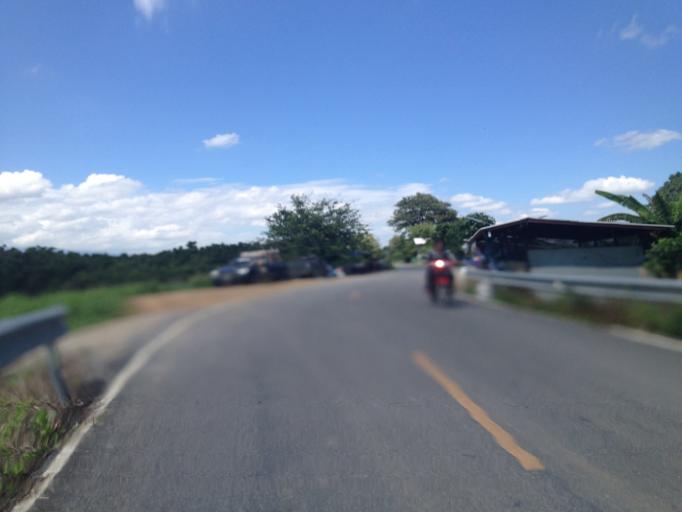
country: TH
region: Chiang Mai
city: San Pa Tong
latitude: 18.6369
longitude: 98.9531
